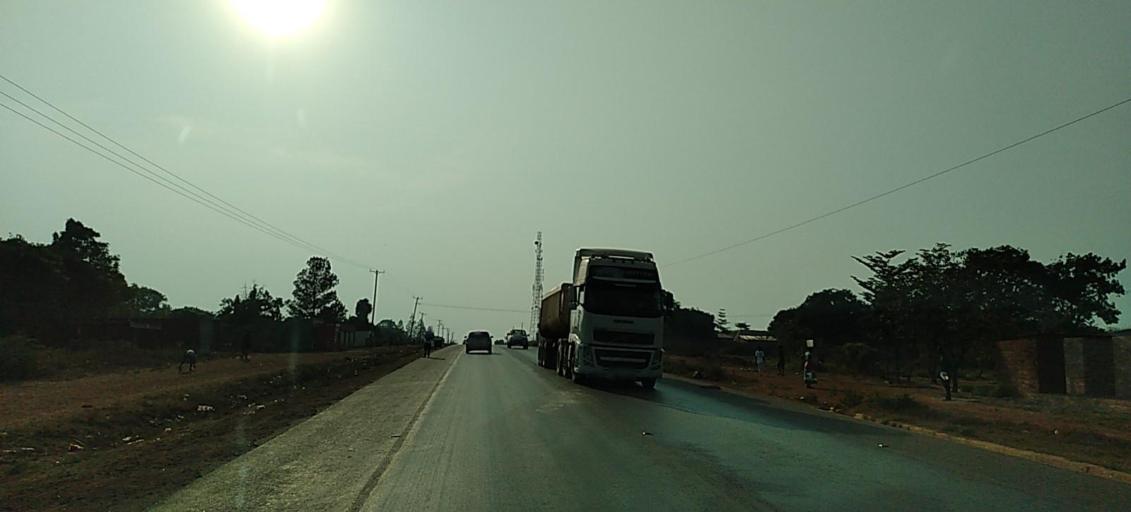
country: ZM
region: North-Western
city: Solwezi
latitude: -12.1915
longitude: 26.4412
